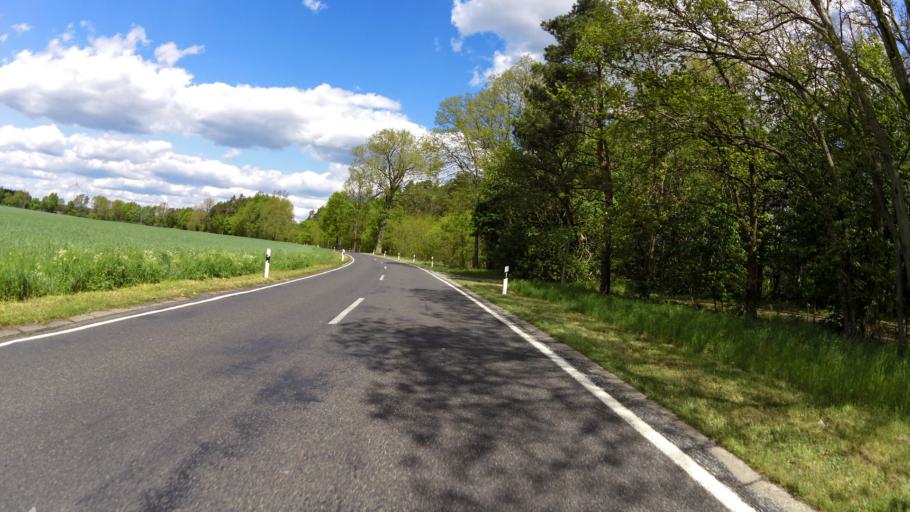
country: DE
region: Brandenburg
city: Diensdorf-Radlow
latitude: 52.1815
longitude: 14.0834
